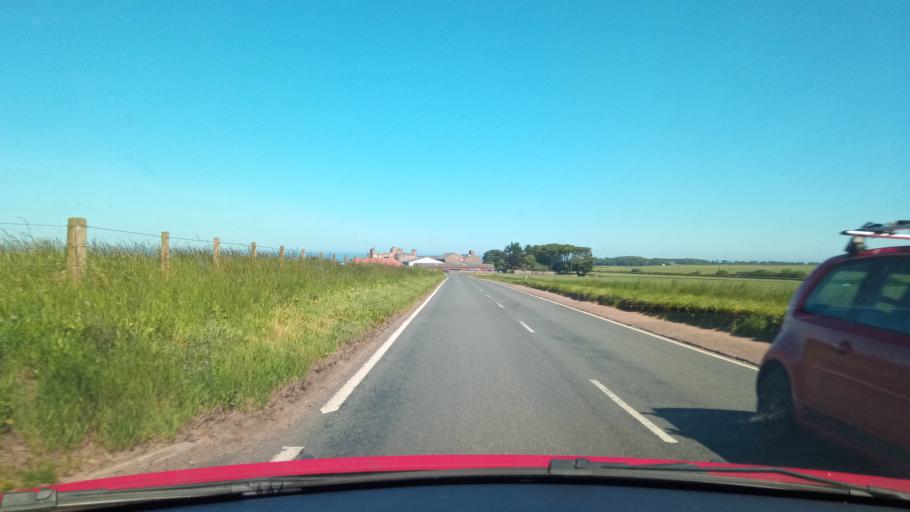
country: GB
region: Scotland
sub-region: East Lothian
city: North Berwick
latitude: 56.0565
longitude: -2.6641
